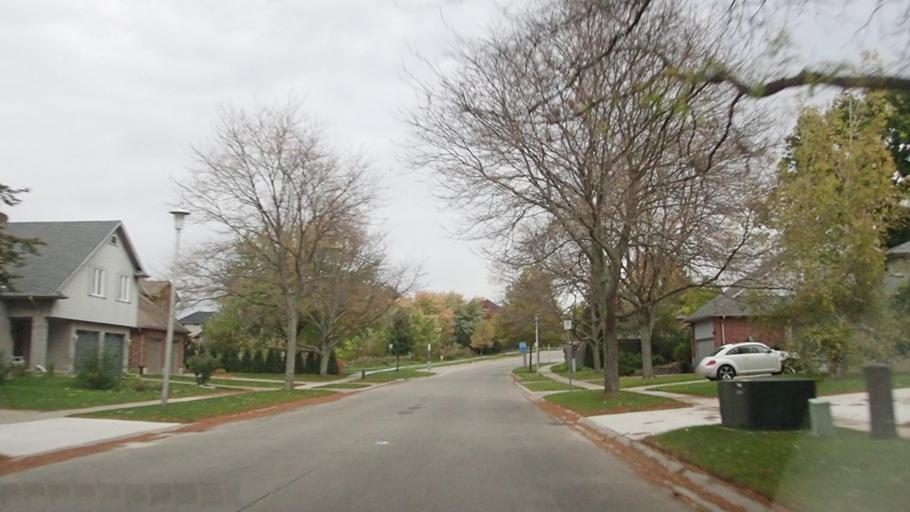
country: CA
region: Ontario
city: London
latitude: 43.0377
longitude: -81.2663
